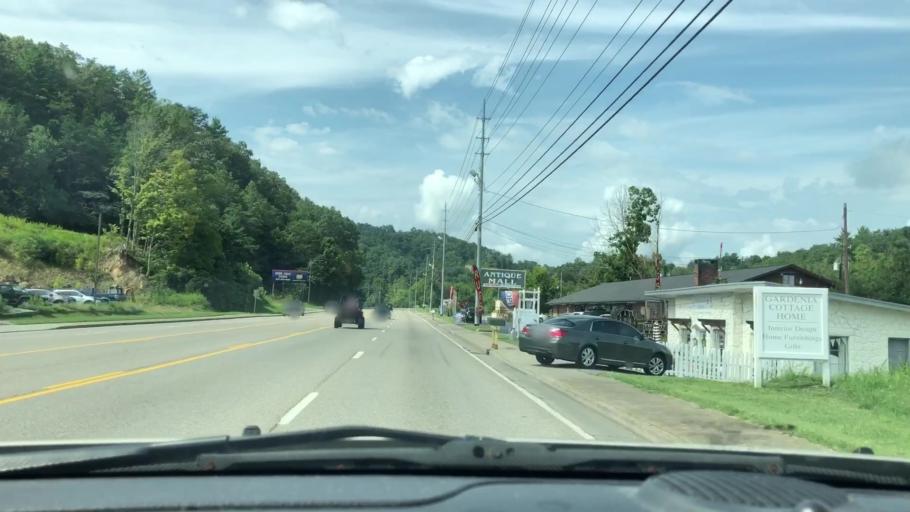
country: US
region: Tennessee
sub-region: Sevier County
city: Pigeon Forge
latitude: 35.7897
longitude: -83.6126
